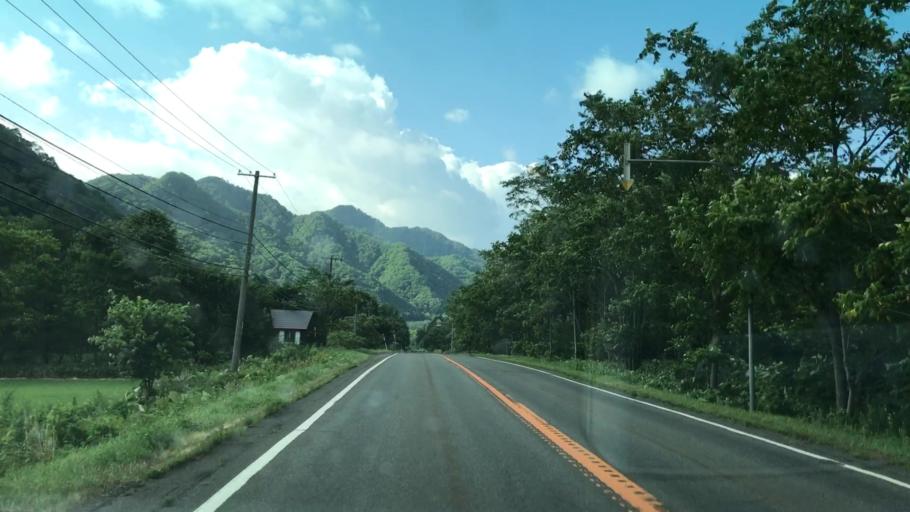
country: JP
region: Hokkaido
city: Shizunai-furukawacho
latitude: 42.8179
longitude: 142.4209
